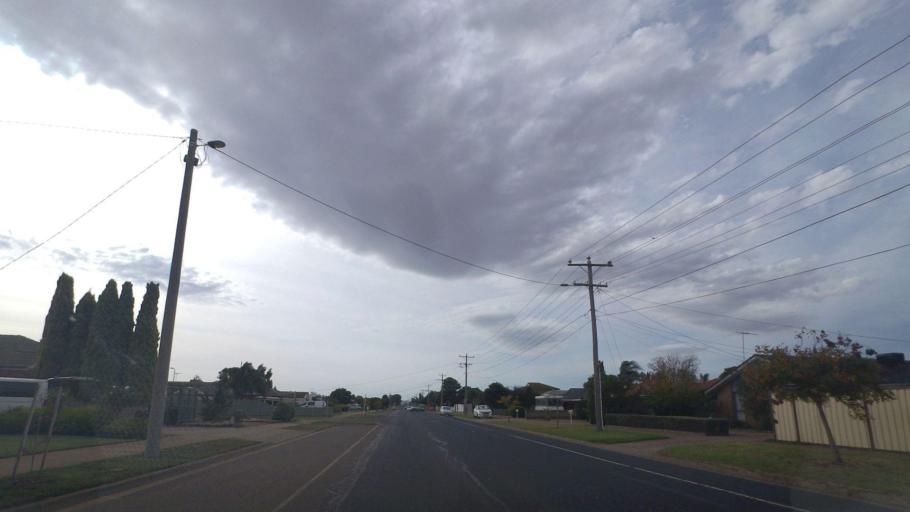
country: AU
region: Victoria
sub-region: Melton
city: Brookfield
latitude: -37.7120
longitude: 144.5629
